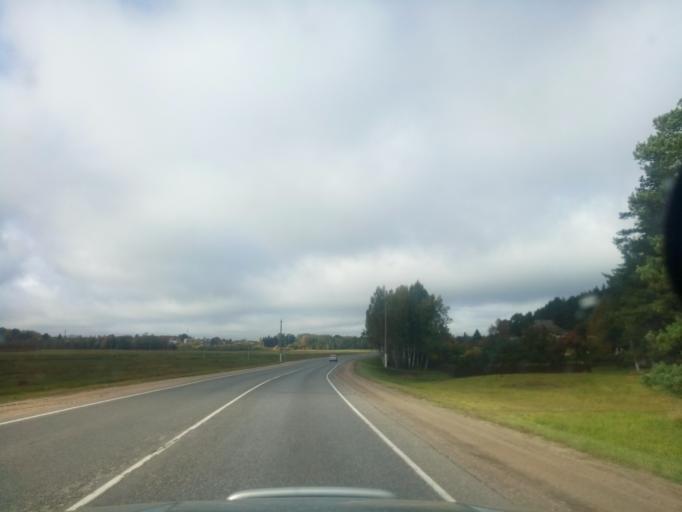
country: BY
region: Minsk
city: Zaslawye
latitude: 53.9932
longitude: 27.2965
